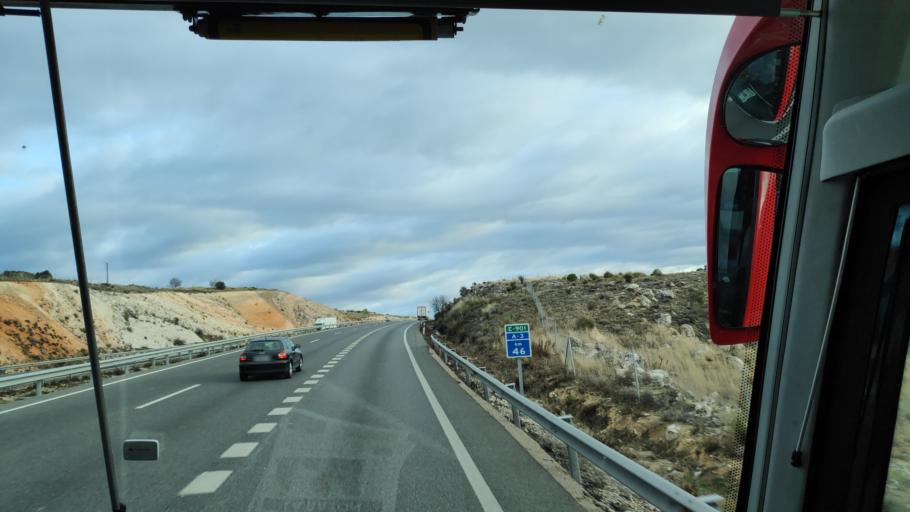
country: ES
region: Madrid
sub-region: Provincia de Madrid
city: Villarejo de Salvanes
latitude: 40.1924
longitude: -3.3011
